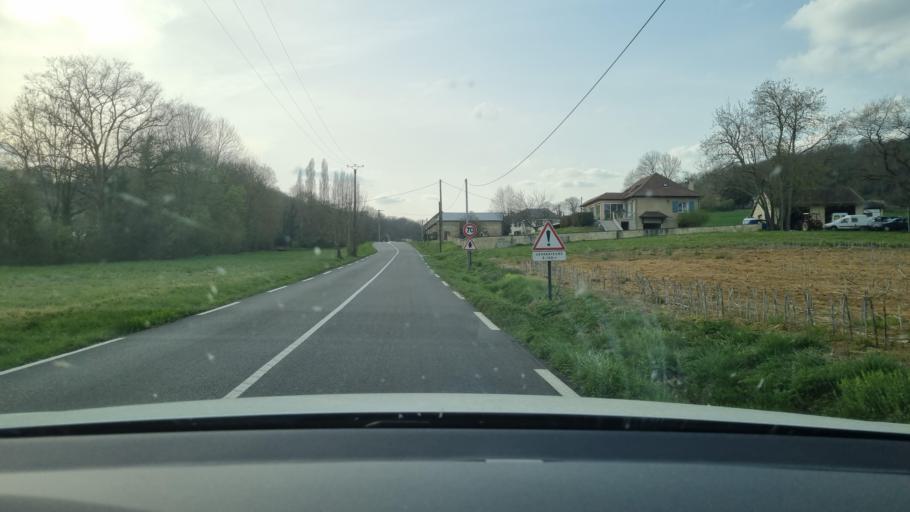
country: FR
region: Aquitaine
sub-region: Departement des Pyrenees-Atlantiques
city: Ger
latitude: 43.3696
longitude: -0.0738
